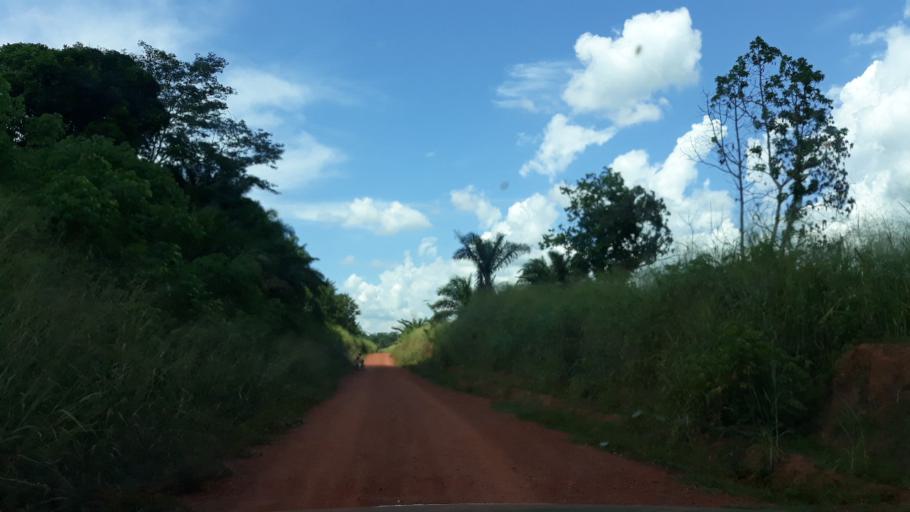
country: CD
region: Equateur
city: Businga
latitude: 3.4046
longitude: 20.3877
